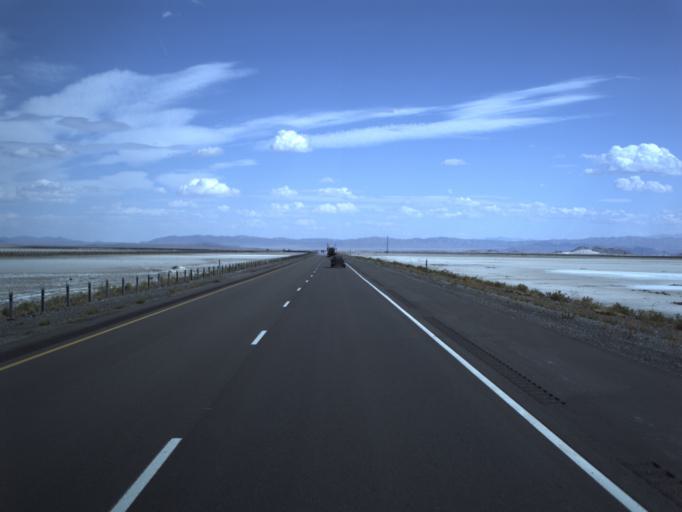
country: US
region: Utah
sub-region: Tooele County
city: Wendover
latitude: 40.7281
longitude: -113.3835
